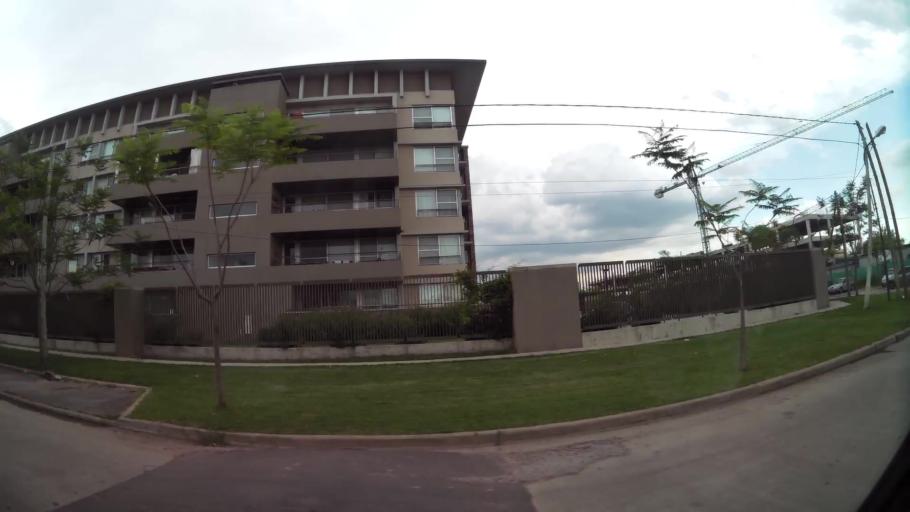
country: AR
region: Buenos Aires
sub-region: Partido de Tigre
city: Tigre
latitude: -34.4819
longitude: -58.5895
